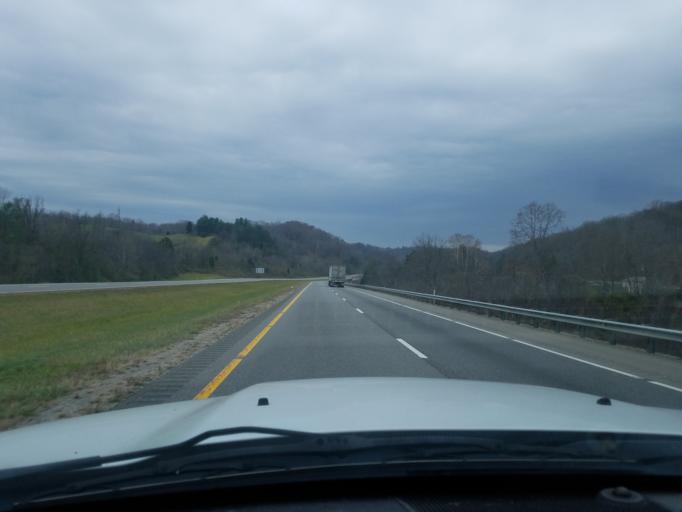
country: US
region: Kentucky
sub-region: Boyd County
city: Catlettsburg
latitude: 38.3810
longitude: -82.6252
